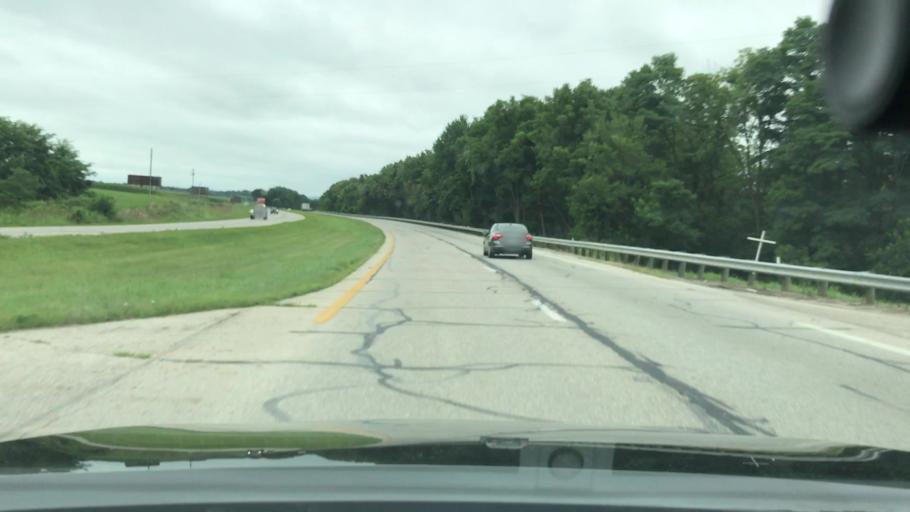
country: US
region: Ohio
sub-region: Ross County
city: Kingston
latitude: 39.4965
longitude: -82.9744
